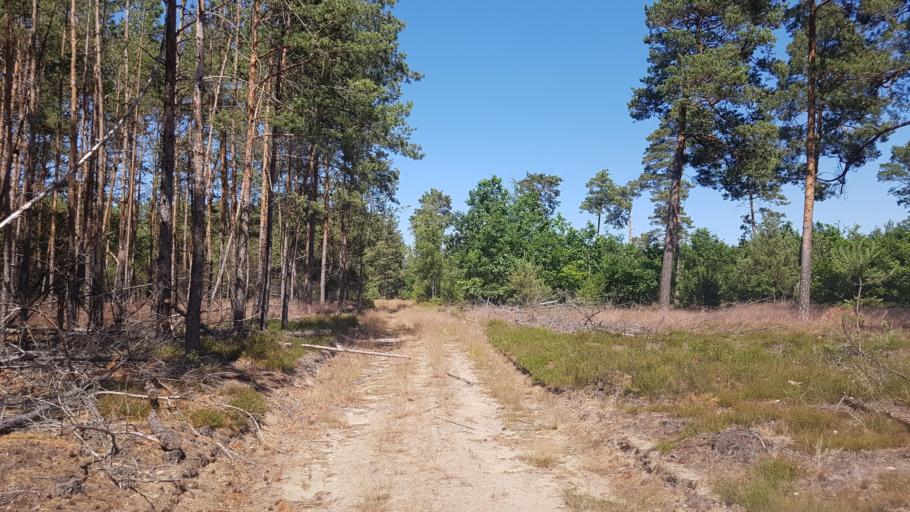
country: DE
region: Brandenburg
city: Treuenbrietzen
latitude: 52.0451
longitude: 12.8402
